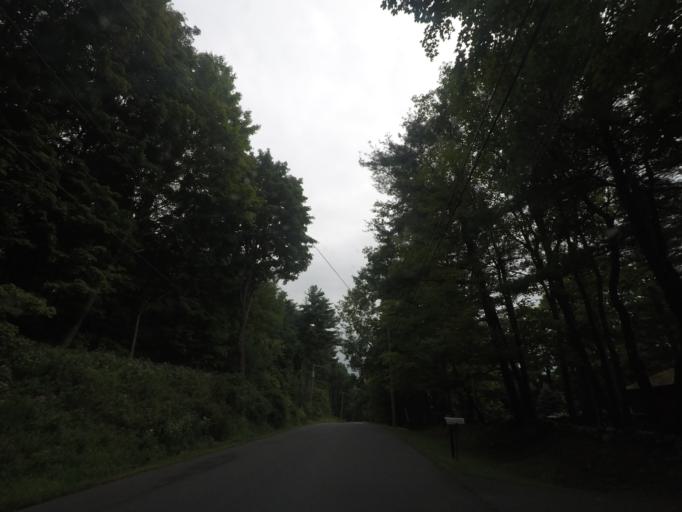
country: US
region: New York
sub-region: Rensselaer County
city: Nassau
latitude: 42.5062
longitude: -73.6077
